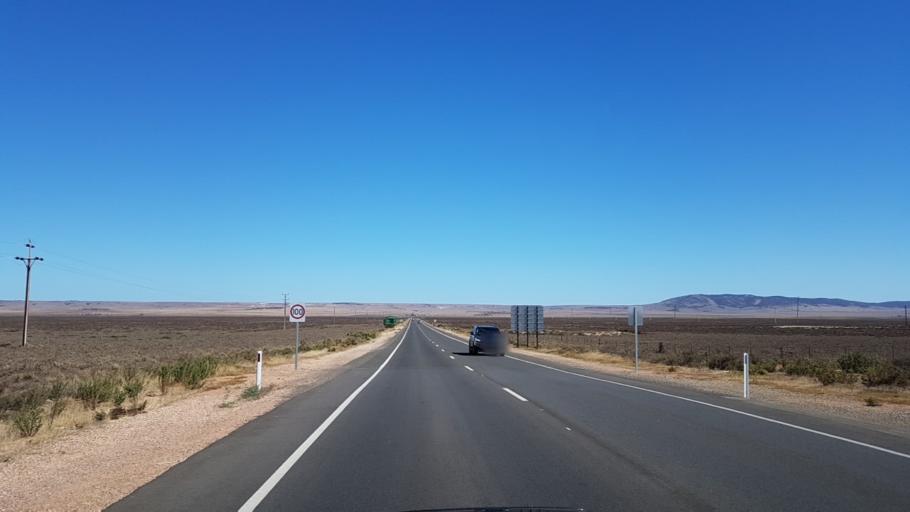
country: AU
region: South Australia
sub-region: Wakefield
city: Balaklava
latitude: -34.1149
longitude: 138.1253
